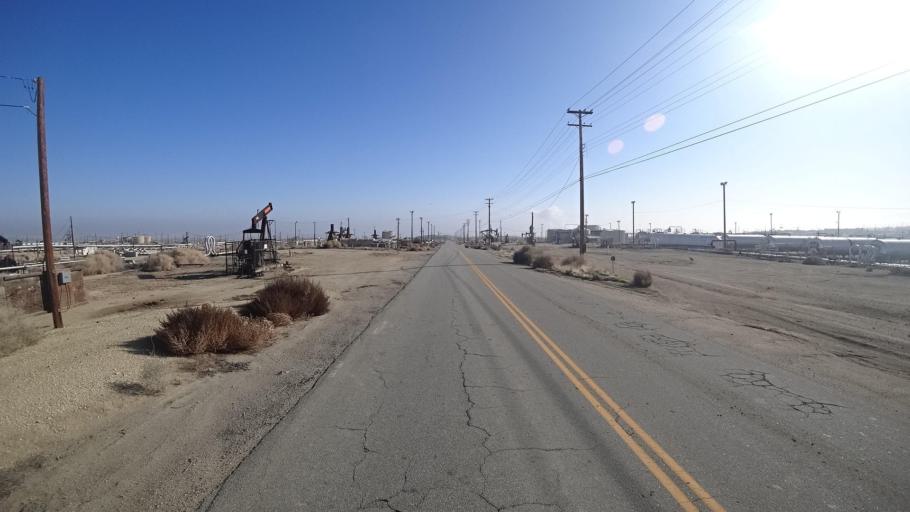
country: US
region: California
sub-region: Kern County
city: Taft Heights
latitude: 35.2232
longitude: -119.6191
